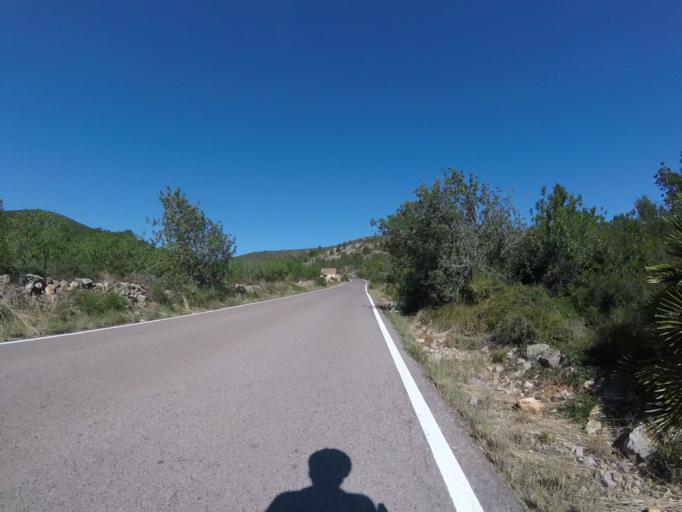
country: ES
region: Valencia
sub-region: Provincia de Castello
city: Santa Magdalena de Pulpis
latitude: 40.3825
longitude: 0.2623
